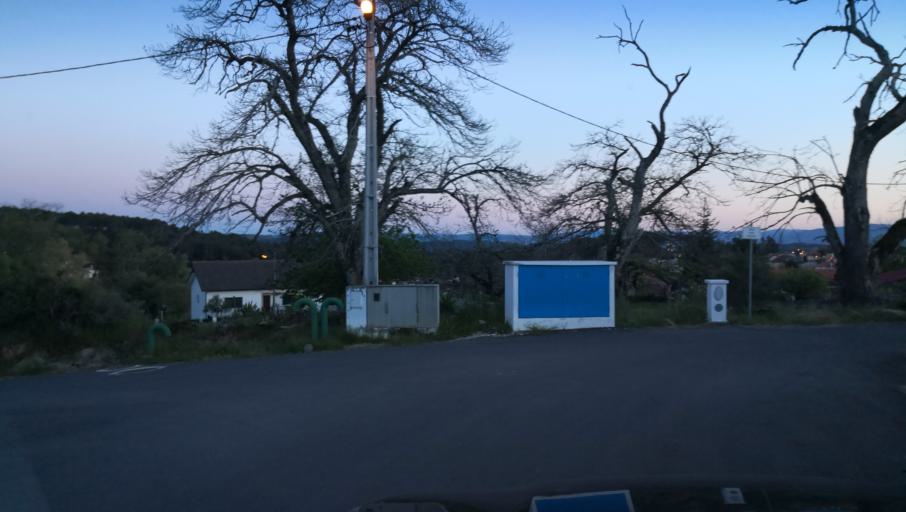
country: PT
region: Vila Real
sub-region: Vila Real
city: Vila Real
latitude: 41.2940
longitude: -7.6768
